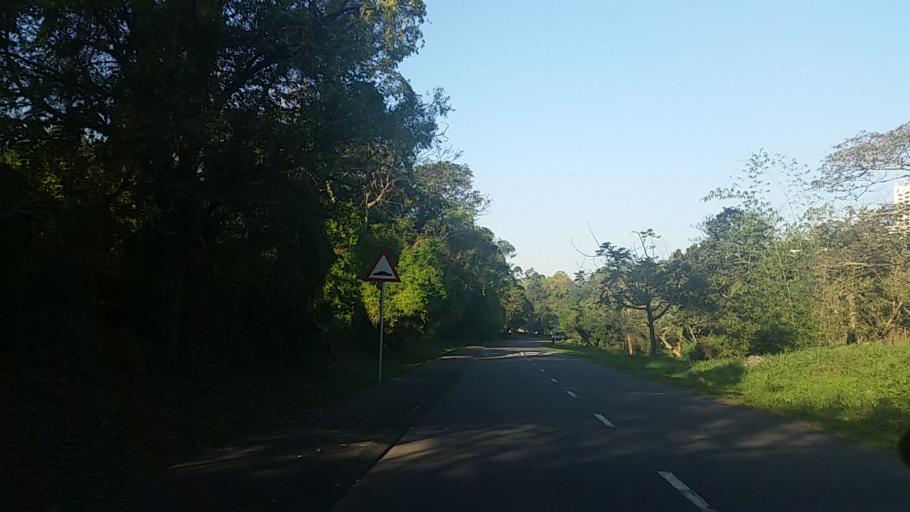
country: ZA
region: KwaZulu-Natal
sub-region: eThekwini Metropolitan Municipality
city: Berea
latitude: -29.8329
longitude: 30.8846
